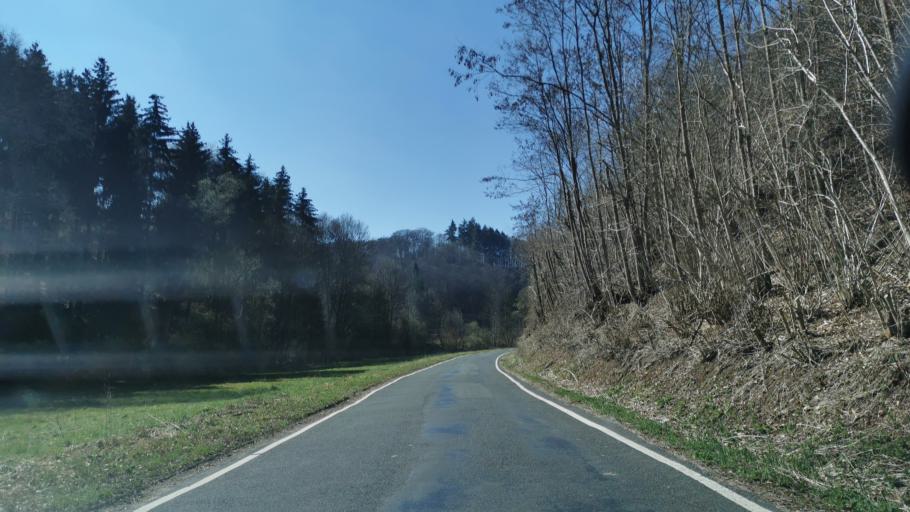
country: DE
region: Rheinland-Pfalz
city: Aach
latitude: 49.7843
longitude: 6.6020
